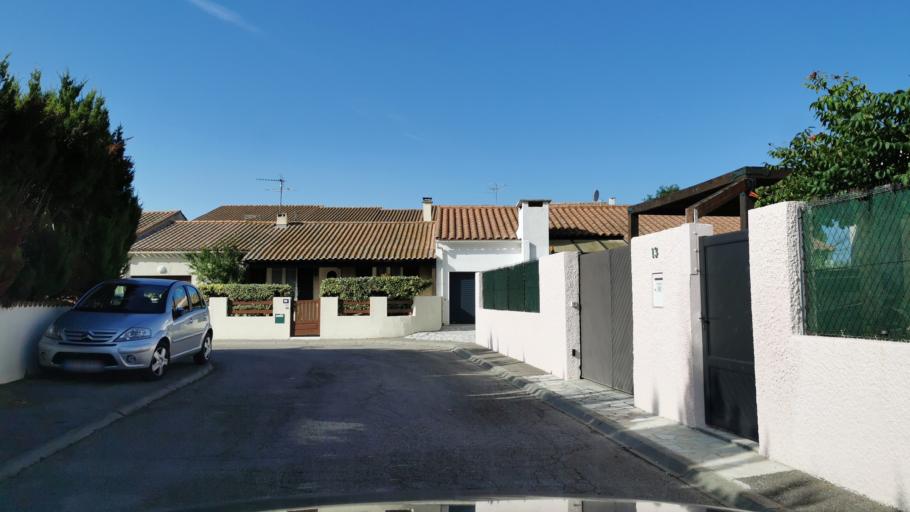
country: FR
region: Languedoc-Roussillon
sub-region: Departement de l'Aude
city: Narbonne
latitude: 43.1740
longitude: 3.0104
